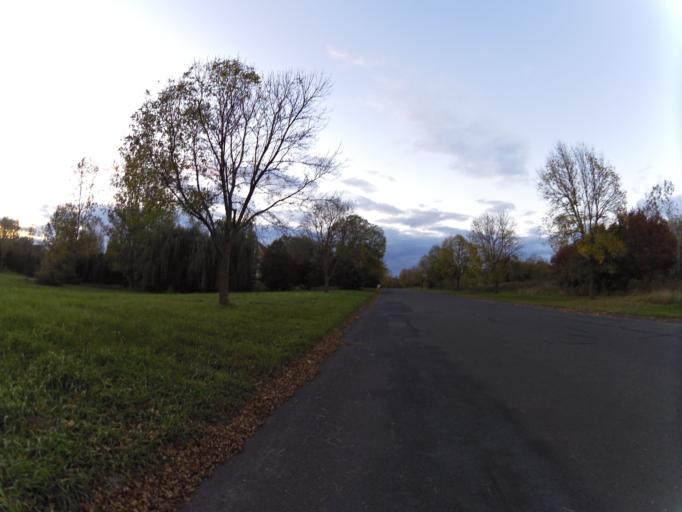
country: US
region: Minnesota
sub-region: Washington County
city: Lakeland
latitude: 44.9587
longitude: -92.8215
